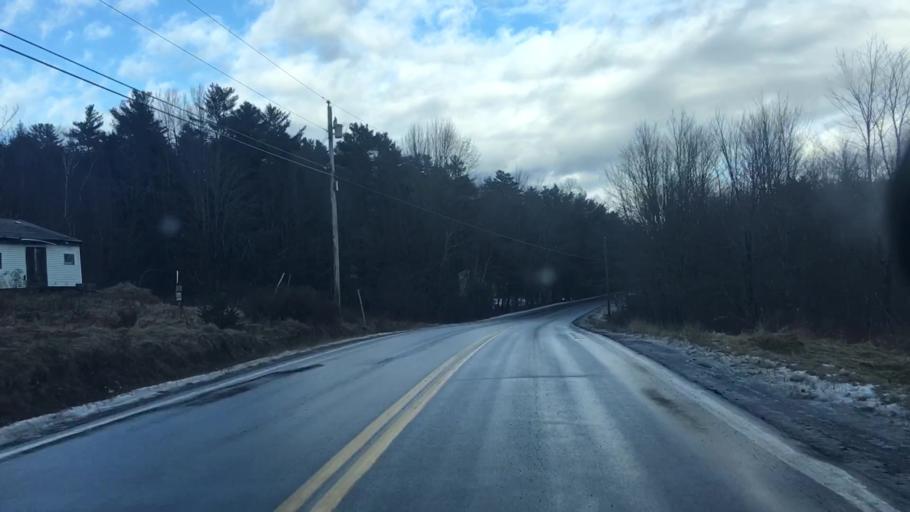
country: US
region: Maine
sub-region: Hancock County
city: Dedham
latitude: 44.6416
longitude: -68.6969
